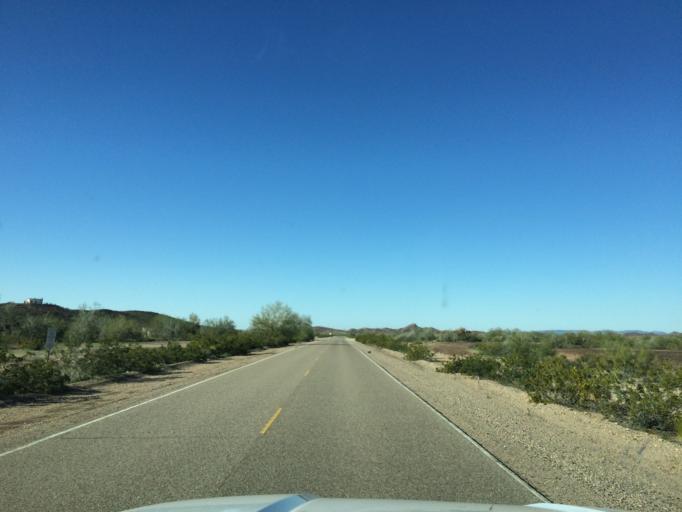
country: US
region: Arizona
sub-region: Yuma County
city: Wellton
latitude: 32.9688
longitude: -114.2852
